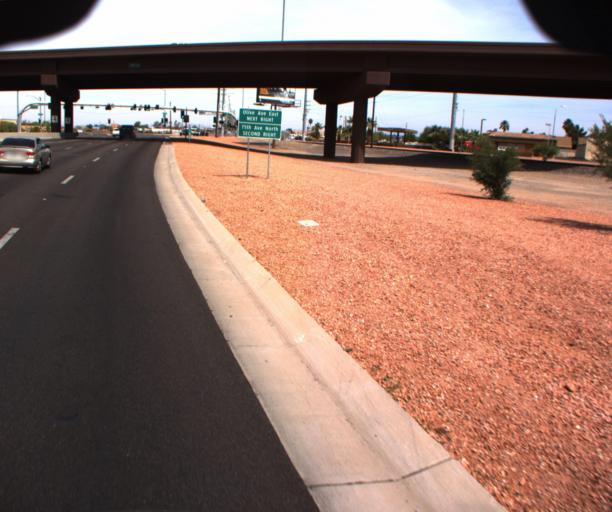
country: US
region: Arizona
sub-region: Maricopa County
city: Peoria
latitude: 33.5658
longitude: -112.2194
